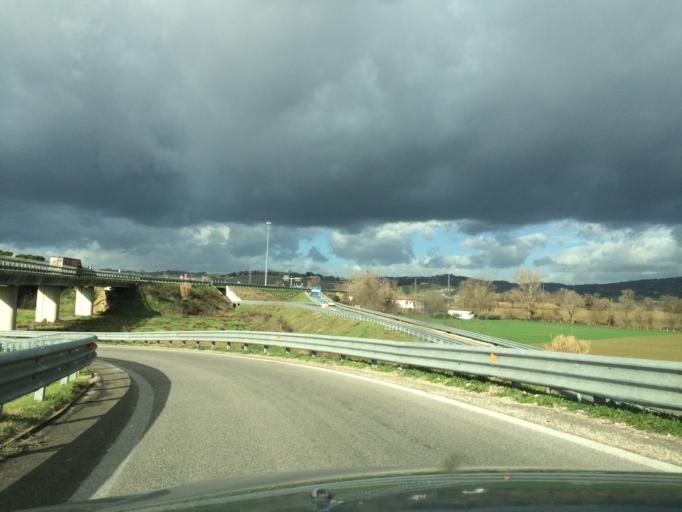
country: IT
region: Umbria
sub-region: Provincia di Terni
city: San Gemini
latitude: 42.5694
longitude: 12.5780
